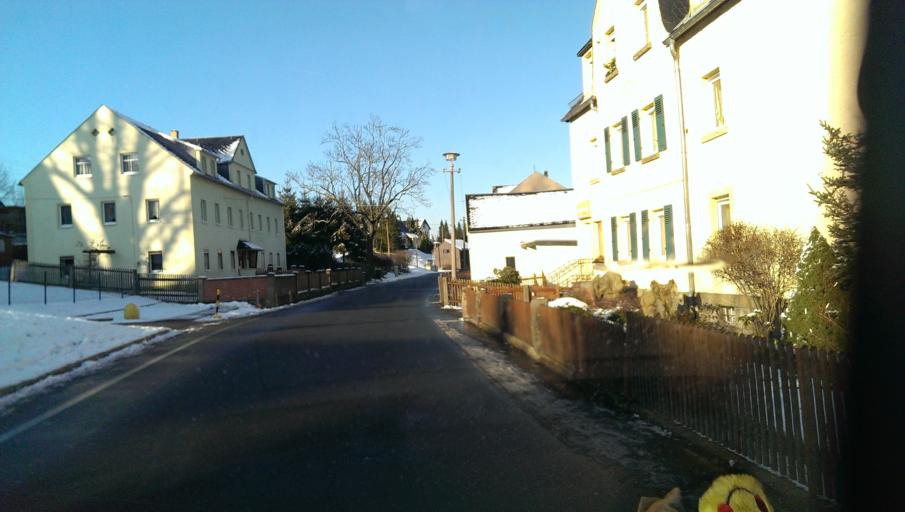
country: DE
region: Saxony
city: Dorfhain
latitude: 50.9291
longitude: 13.5866
